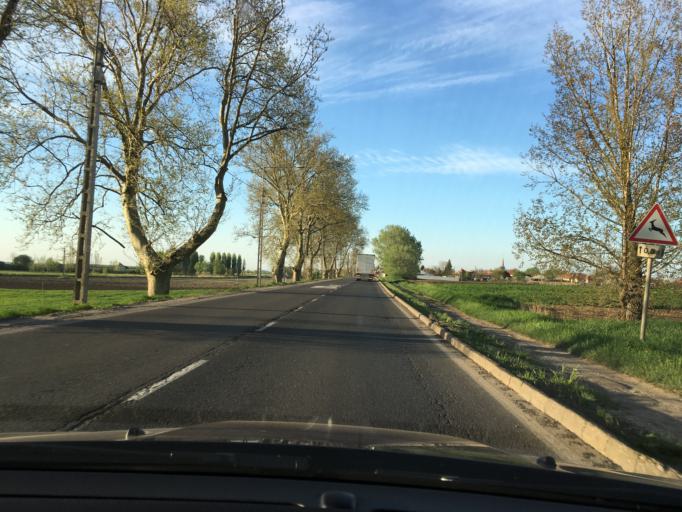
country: HU
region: Hajdu-Bihar
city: Mikepercs
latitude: 47.4317
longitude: 21.6269
